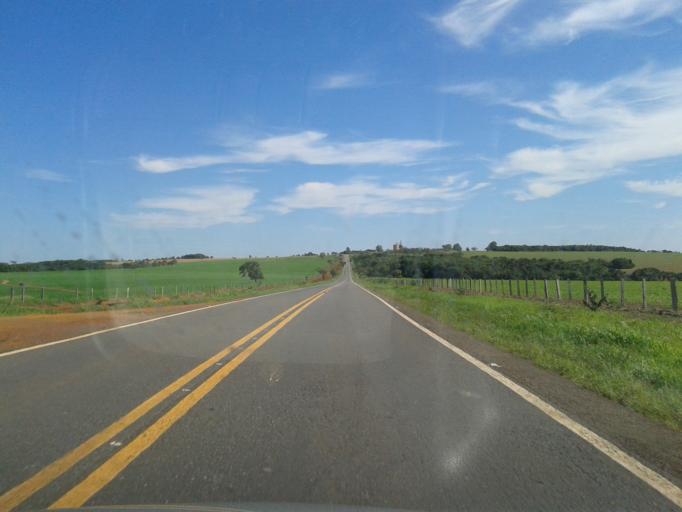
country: BR
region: Goias
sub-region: Piracanjuba
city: Piracanjuba
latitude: -17.3536
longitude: -48.7946
